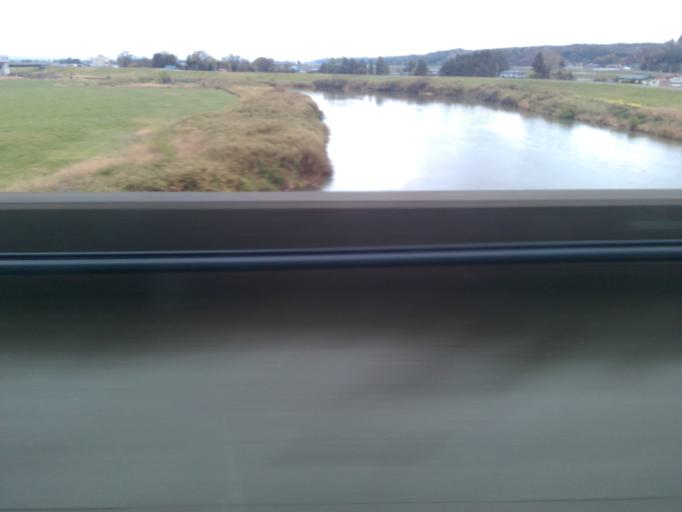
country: JP
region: Miyagi
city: Furukawa
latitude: 38.5250
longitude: 140.9604
